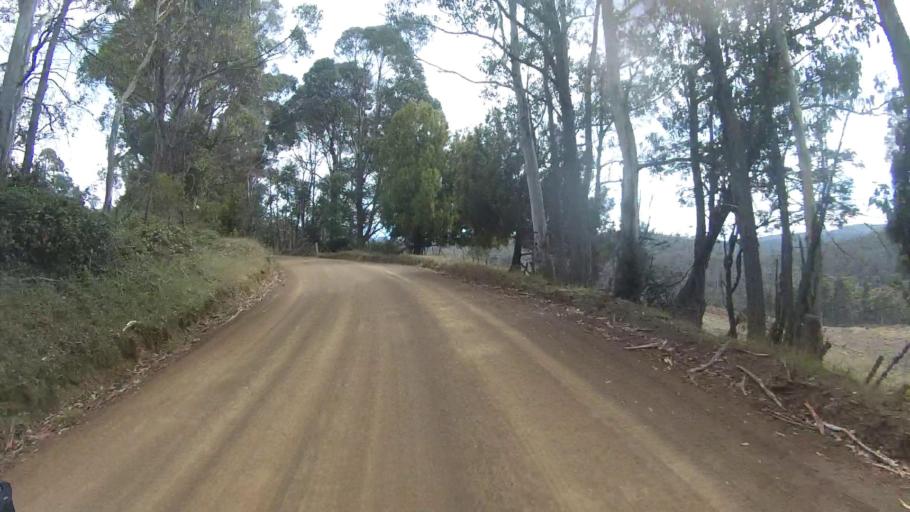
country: AU
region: Tasmania
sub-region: Sorell
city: Sorell
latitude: -42.7316
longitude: 147.7599
